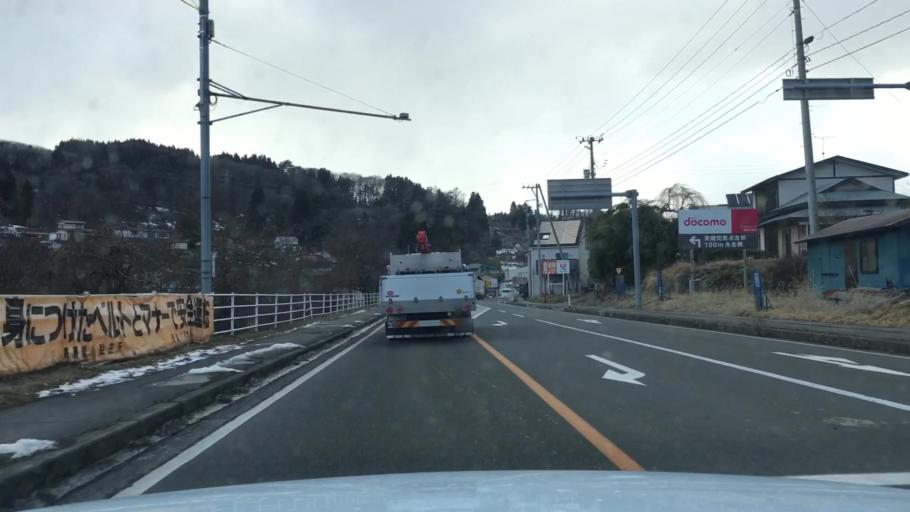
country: JP
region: Iwate
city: Morioka-shi
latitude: 39.6806
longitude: 141.1853
